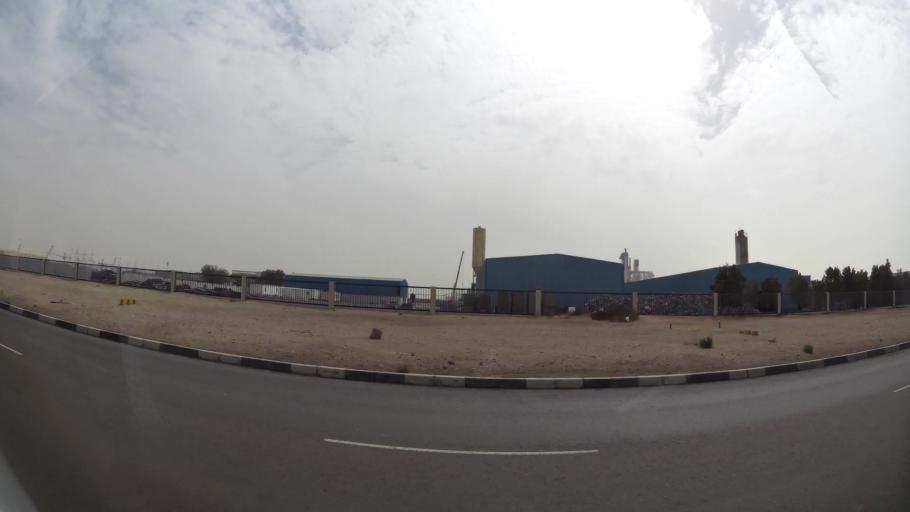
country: AE
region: Abu Dhabi
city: Abu Dhabi
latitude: 24.3232
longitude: 54.5022
